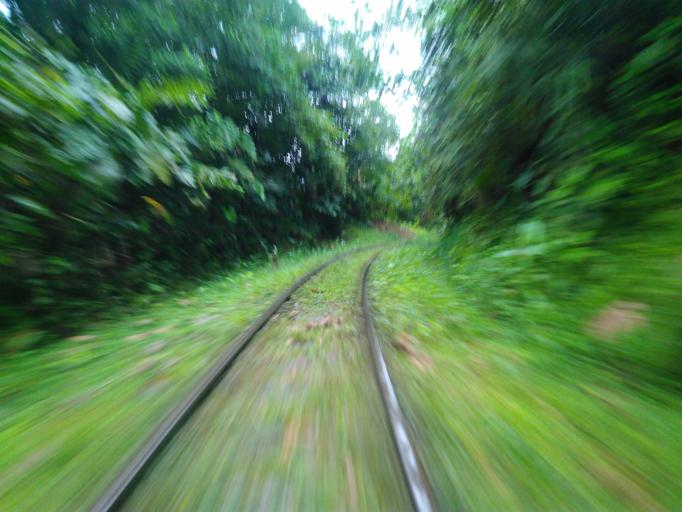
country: CO
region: Valle del Cauca
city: Buenaventura
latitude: 3.8440
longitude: -76.8770
